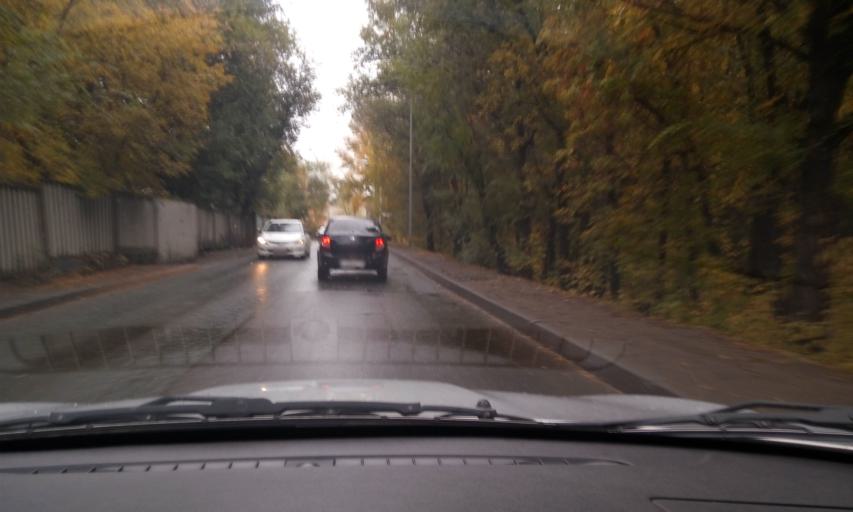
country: KZ
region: Astana Qalasy
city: Astana
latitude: 51.1433
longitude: 71.4313
